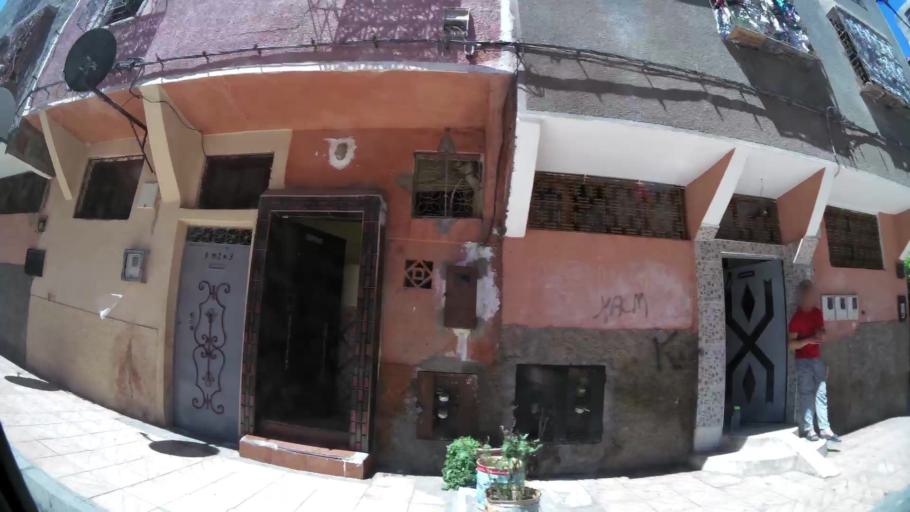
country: MA
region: Marrakech-Tensift-Al Haouz
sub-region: Marrakech
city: Marrakesh
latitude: 31.6540
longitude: -7.9917
